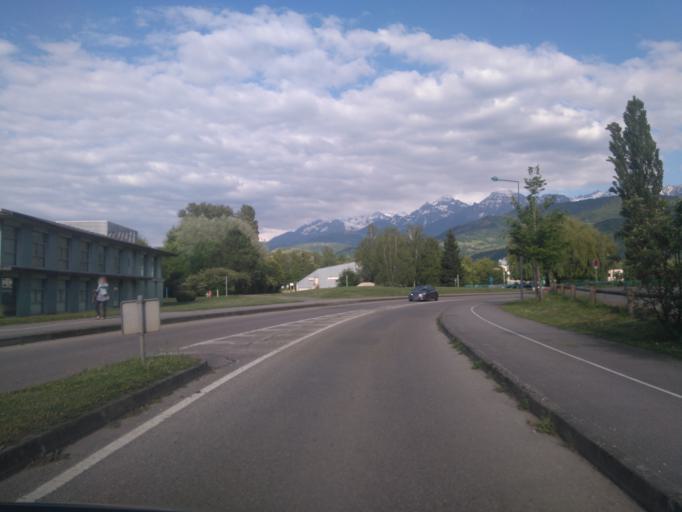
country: FR
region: Rhone-Alpes
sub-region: Departement de l'Isere
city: Gieres
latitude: 45.1922
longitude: 5.7767
